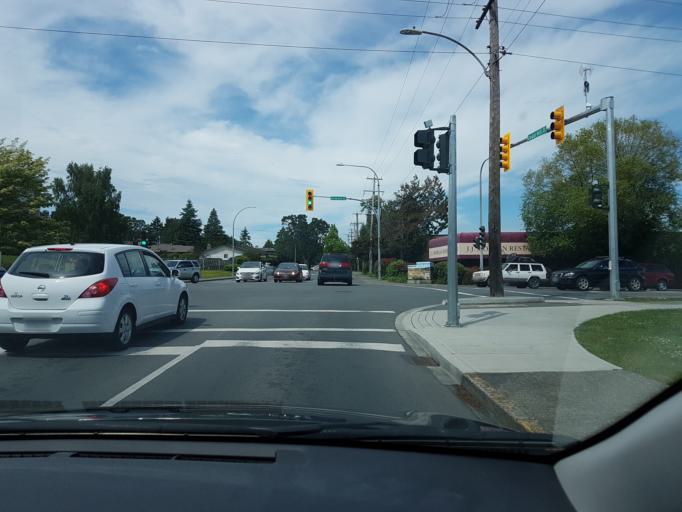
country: CA
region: British Columbia
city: Oak Bay
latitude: 48.4685
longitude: -123.3354
